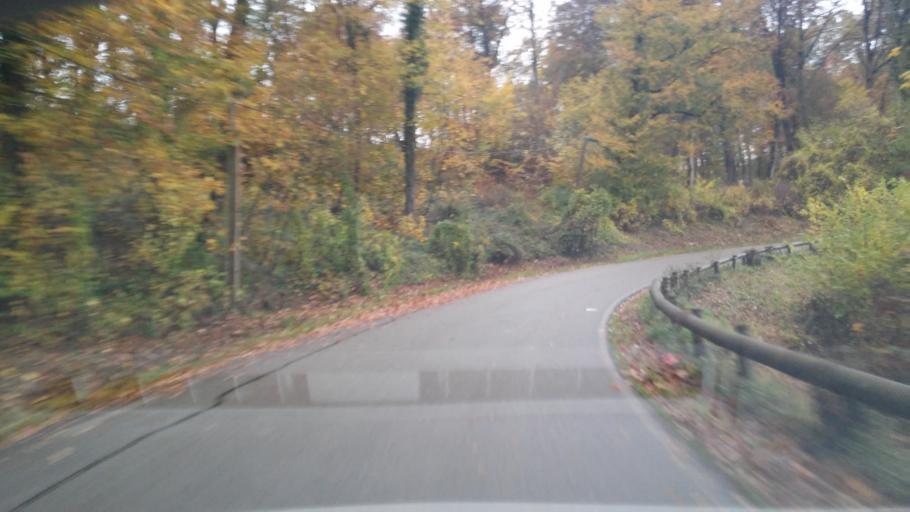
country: FR
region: Lorraine
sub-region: Departement de la Moselle
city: Courcelles-Chaussy
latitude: 49.1925
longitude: 6.3980
